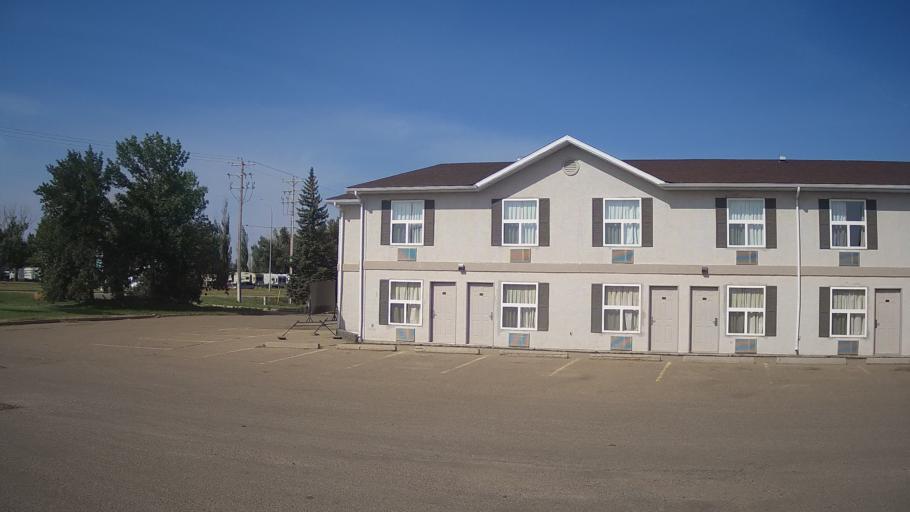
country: CA
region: Alberta
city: Brooks
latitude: 50.5725
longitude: -111.8685
